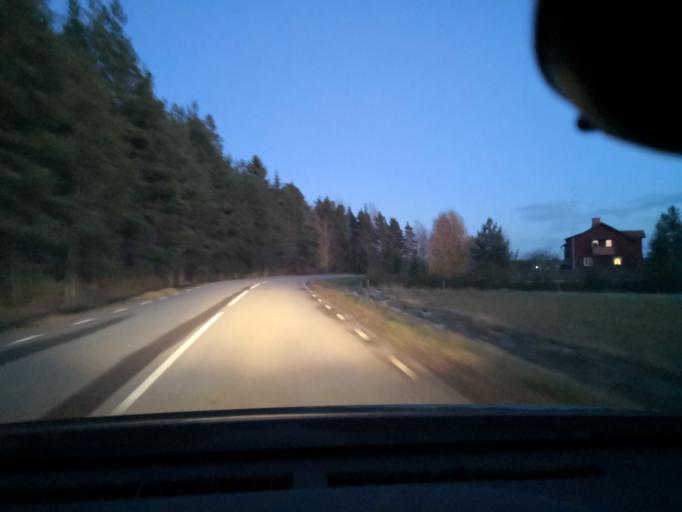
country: SE
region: Vaestmanland
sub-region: Sala Kommun
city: Sala
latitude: 59.8725
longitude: 16.7053
